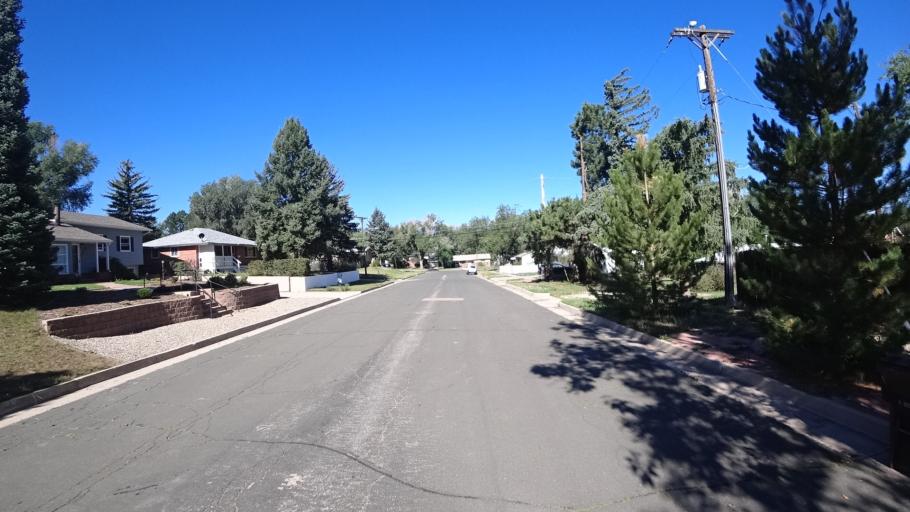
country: US
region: Colorado
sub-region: El Paso County
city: Colorado Springs
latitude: 38.8516
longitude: -104.7831
